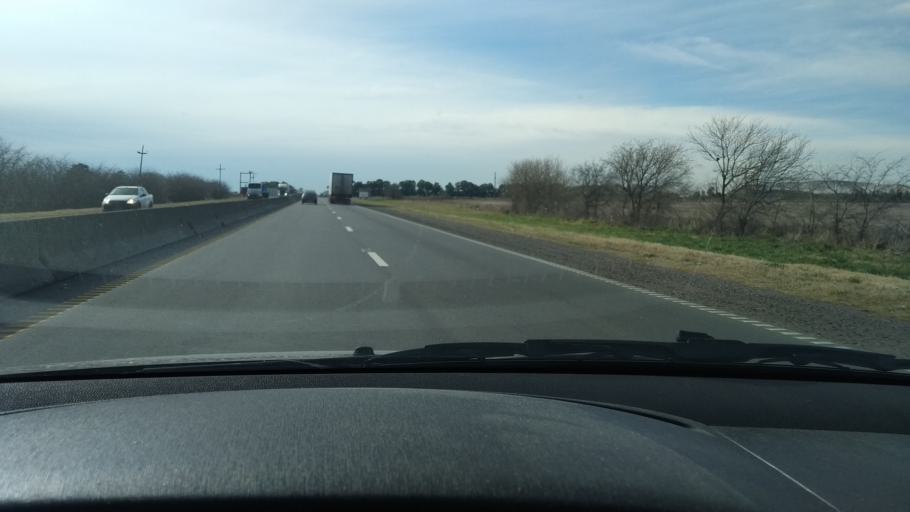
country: AR
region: Buenos Aires
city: Olavarria
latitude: -36.9264
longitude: -60.2171
